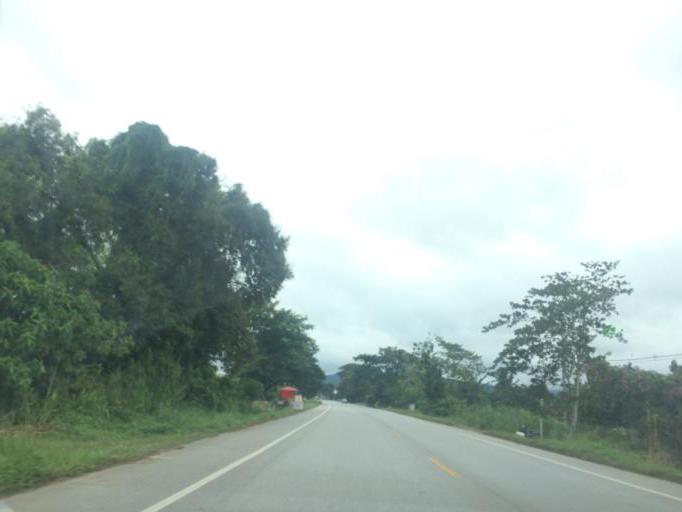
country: TH
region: Chiang Rai
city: Mae Lao
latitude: 19.7463
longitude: 99.7142
